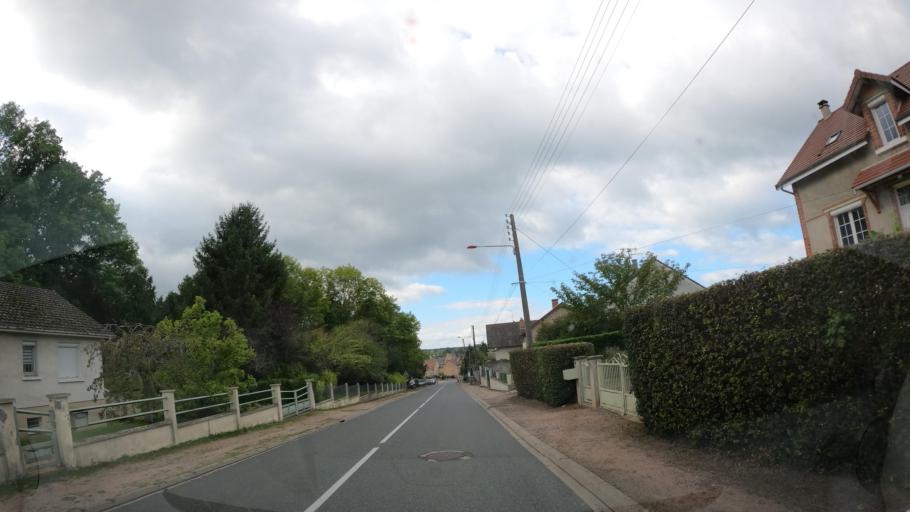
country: FR
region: Auvergne
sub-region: Departement de l'Allier
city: Lapalisse
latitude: 46.3787
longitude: 3.5955
